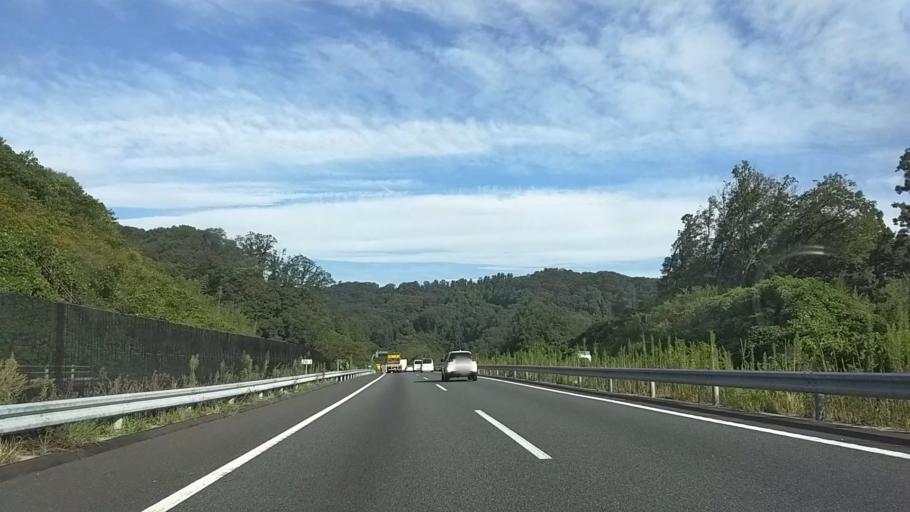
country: JP
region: Kanagawa
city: Zama
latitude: 35.5555
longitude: 139.3152
